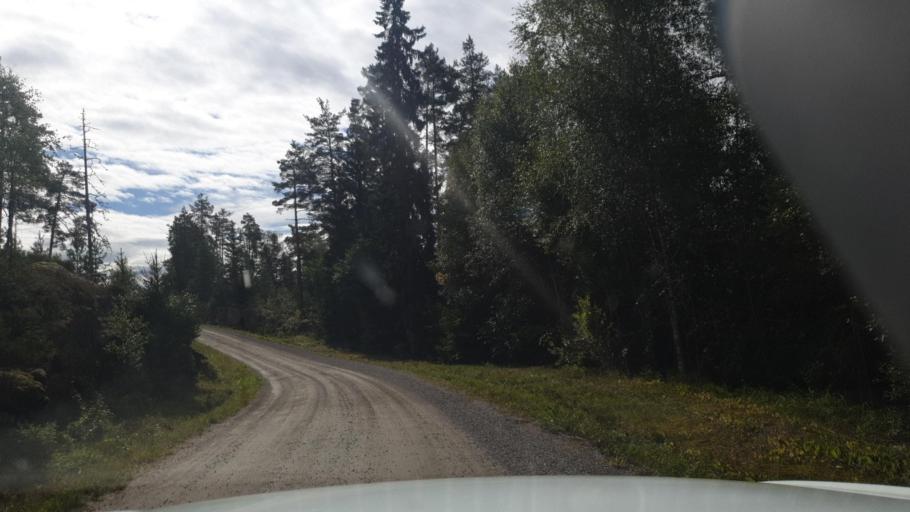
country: SE
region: Vaermland
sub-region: Eda Kommun
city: Charlottenberg
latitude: 60.0408
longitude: 12.5103
